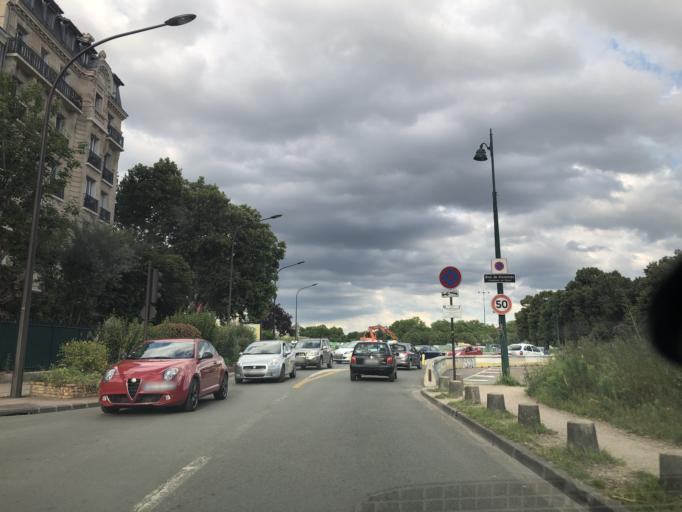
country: FR
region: Ile-de-France
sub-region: Departement du Val-de-Marne
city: Vincennes
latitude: 48.8412
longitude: 2.4325
